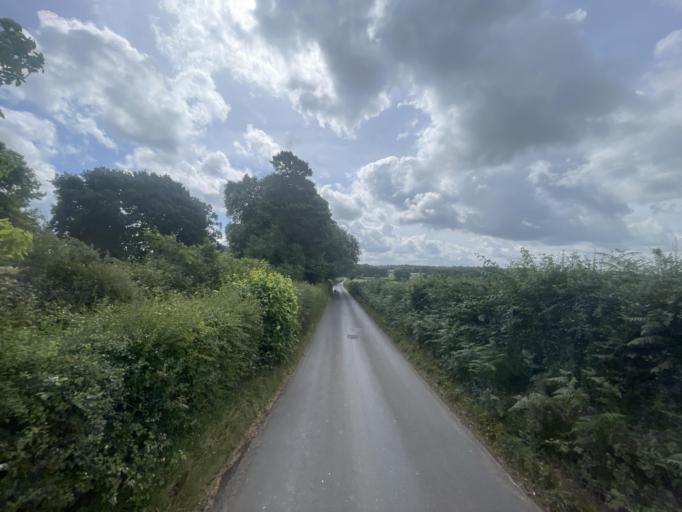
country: GB
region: England
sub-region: Kent
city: Edenbridge
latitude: 51.1602
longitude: 0.1460
